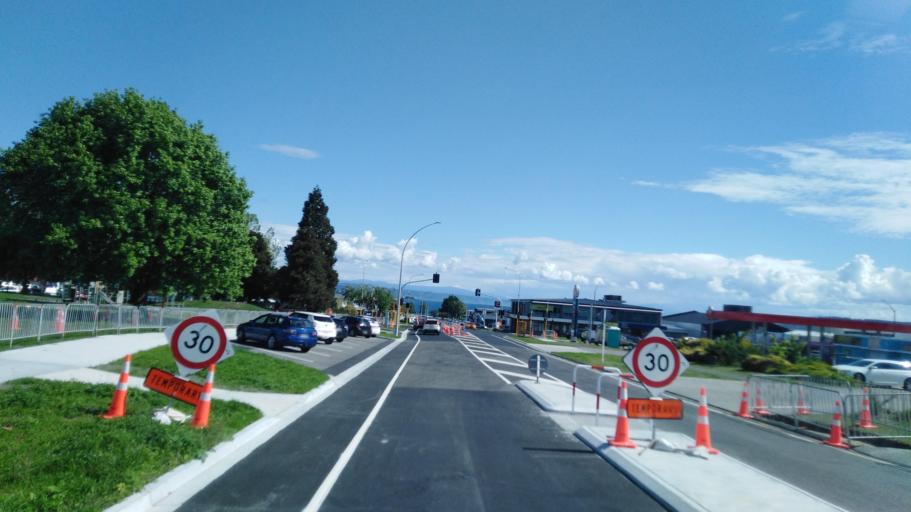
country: NZ
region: Waikato
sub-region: Taupo District
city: Taupo
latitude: -38.6877
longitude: 176.0749
